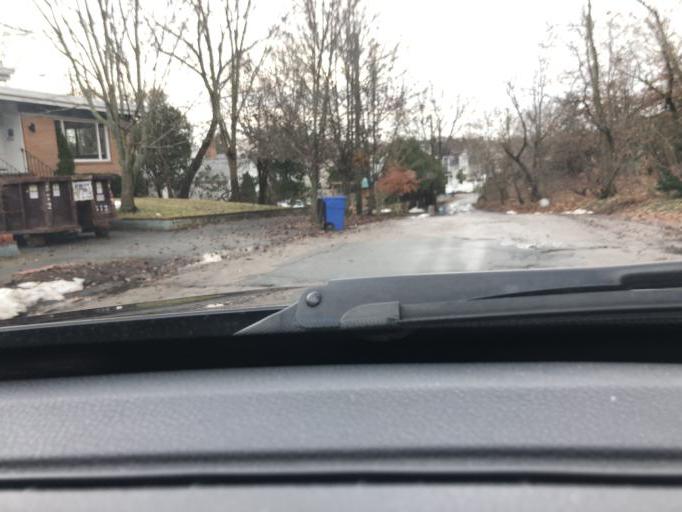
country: US
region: Massachusetts
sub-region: Middlesex County
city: Arlington
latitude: 42.4205
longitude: -71.1571
